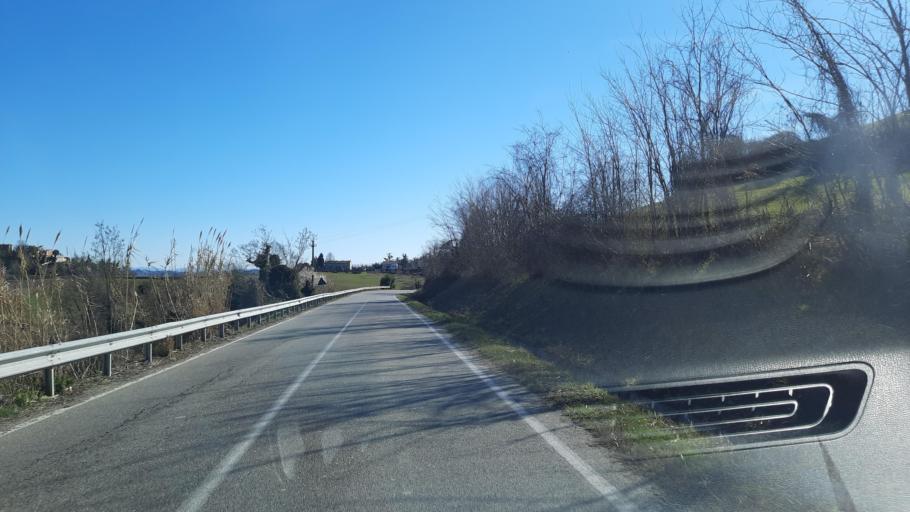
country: IT
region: Piedmont
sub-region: Provincia di Alessandria
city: Rosignano Monferrato
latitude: 45.0869
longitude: 8.4132
